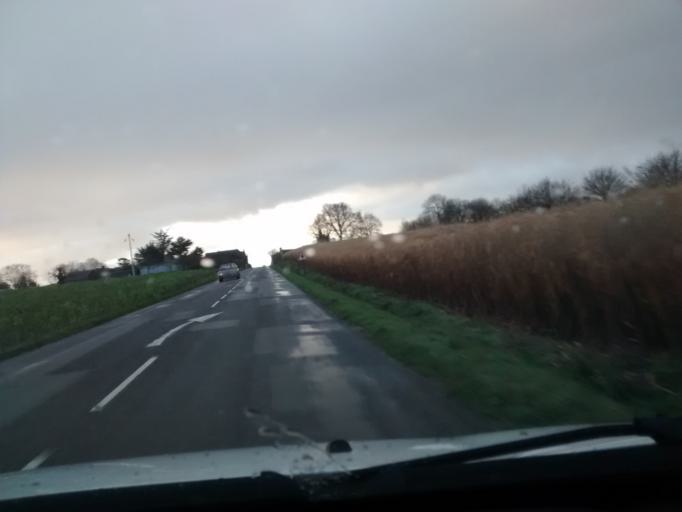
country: FR
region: Brittany
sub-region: Departement d'Ille-et-Vilaine
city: Bais
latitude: 47.9929
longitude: -1.2867
